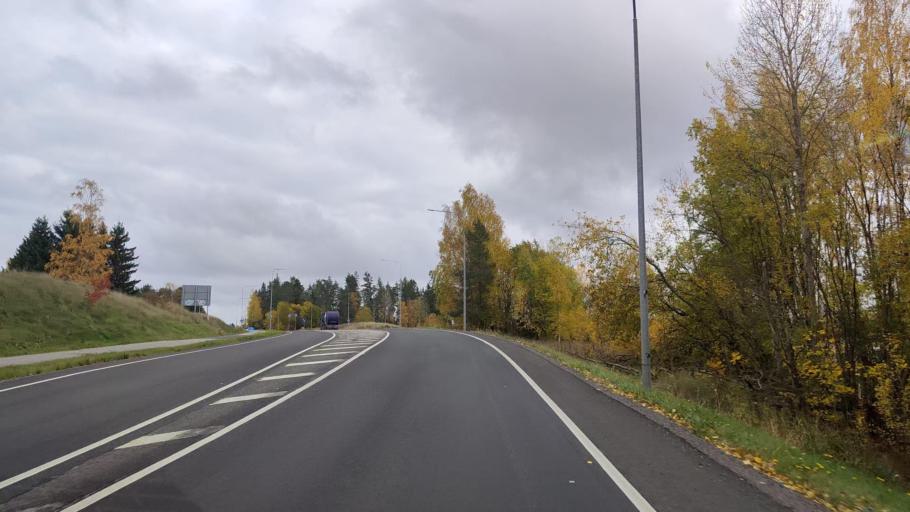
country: FI
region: Varsinais-Suomi
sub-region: Turku
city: Kaarina
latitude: 60.4637
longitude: 22.3512
